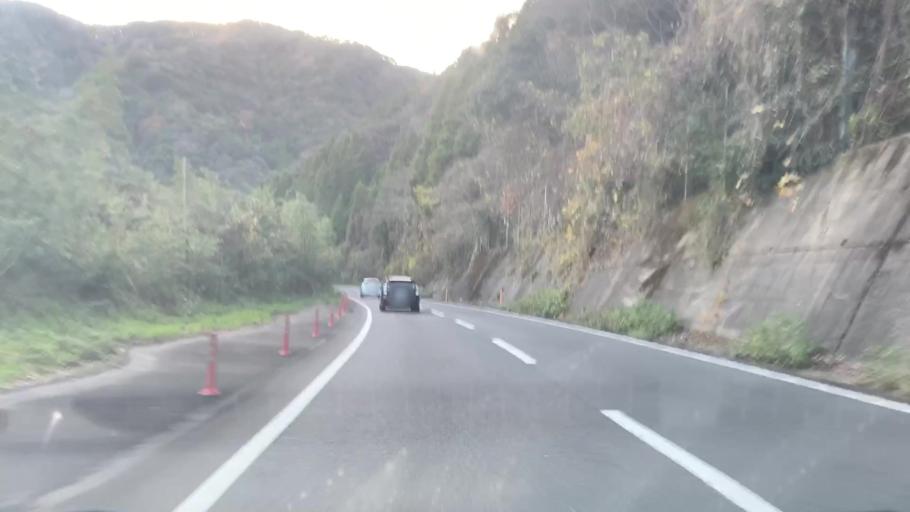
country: JP
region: Saga Prefecture
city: Karatsu
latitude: 33.3369
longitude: 129.9718
